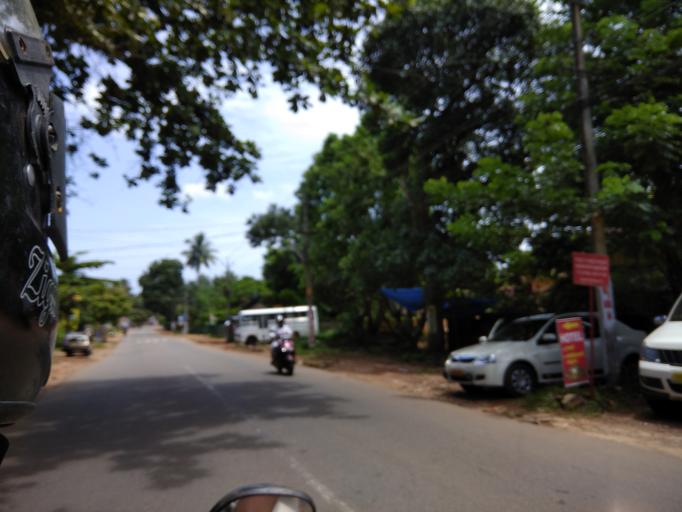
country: IN
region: Kerala
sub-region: Thrissur District
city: Trichur
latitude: 10.4976
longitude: 76.1580
